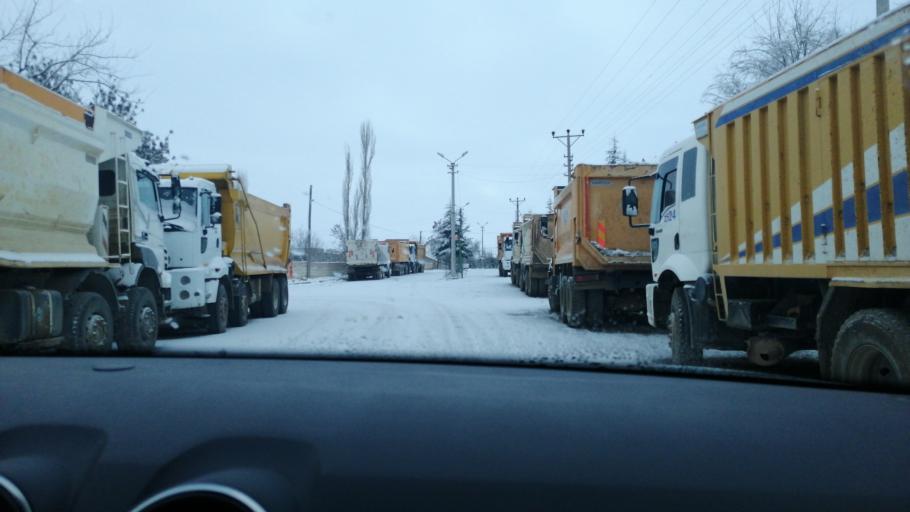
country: TR
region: Aksaray
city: Agacoren
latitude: 38.9311
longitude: 33.9491
